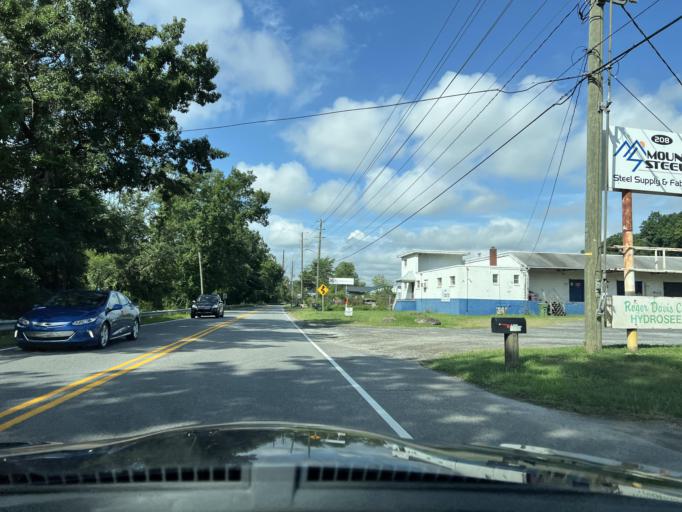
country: US
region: North Carolina
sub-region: Buncombe County
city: Asheville
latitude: 35.5734
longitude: -82.5283
